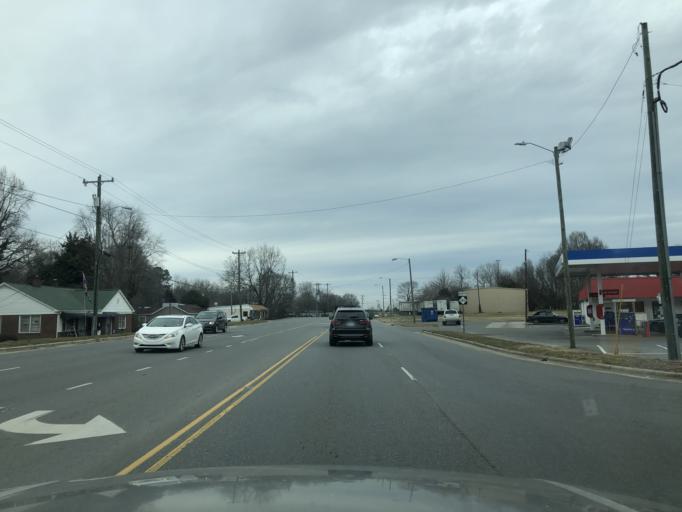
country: US
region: North Carolina
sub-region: Cleveland County
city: Shelby
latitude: 35.2920
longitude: -81.4902
